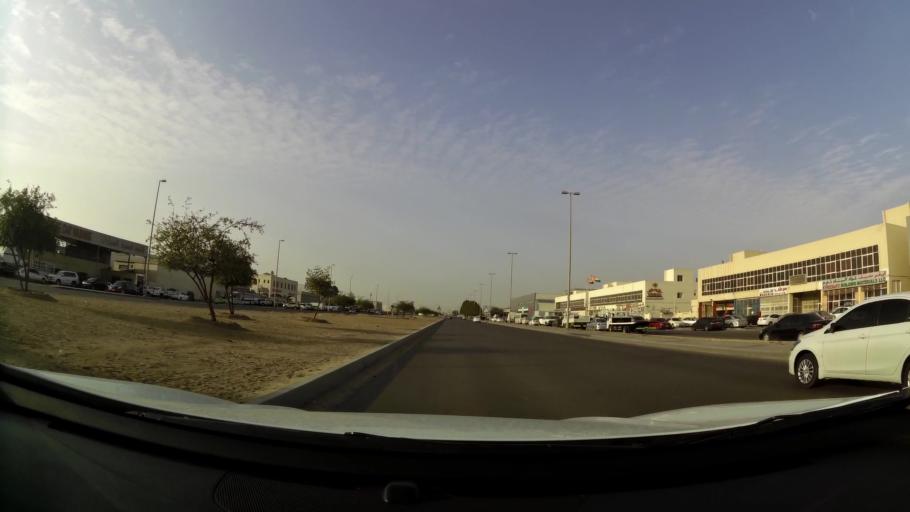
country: AE
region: Abu Dhabi
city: Abu Dhabi
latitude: 24.3653
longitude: 54.5165
